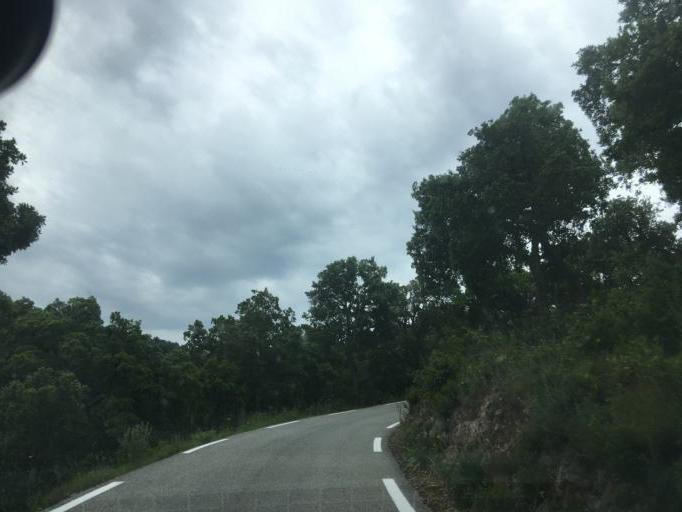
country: FR
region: Provence-Alpes-Cote d'Azur
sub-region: Departement du Var
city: Pierrefeu-du-Var
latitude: 43.2189
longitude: 6.2188
